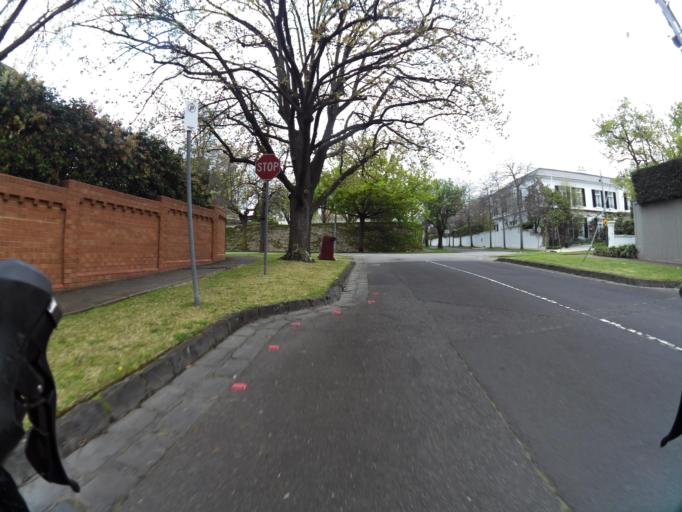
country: AU
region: Victoria
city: Toorak
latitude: -37.8454
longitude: 145.0237
